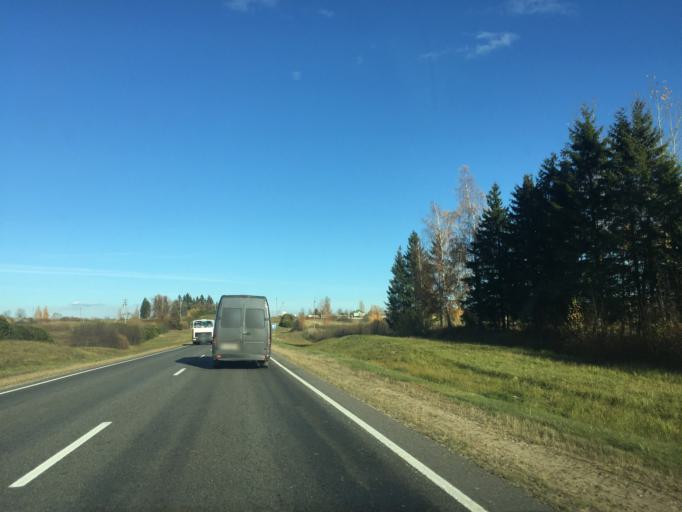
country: BY
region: Vitebsk
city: Dzisna
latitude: 55.2970
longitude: 28.2072
